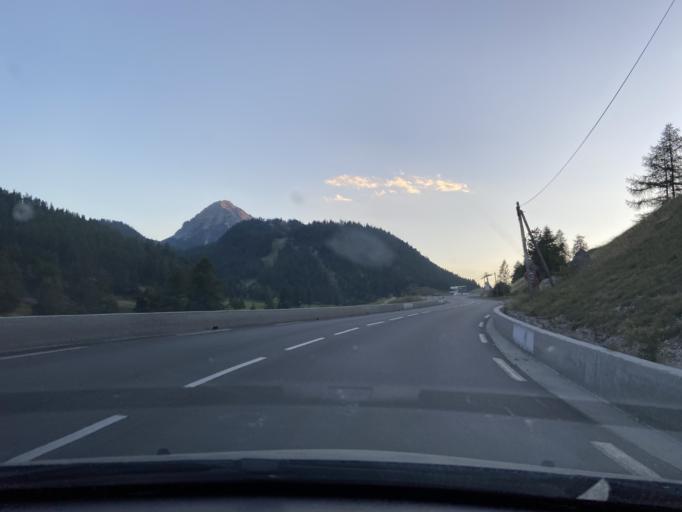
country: IT
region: Piedmont
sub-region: Provincia di Torino
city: Claviere
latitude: 44.9342
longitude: 6.7419
